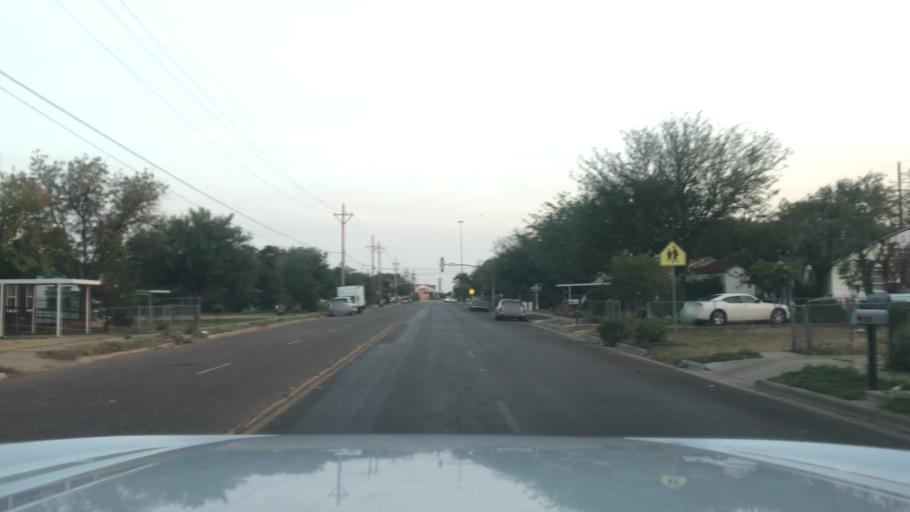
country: US
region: Texas
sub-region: Lubbock County
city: Lubbock
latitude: 33.5976
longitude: -101.8619
